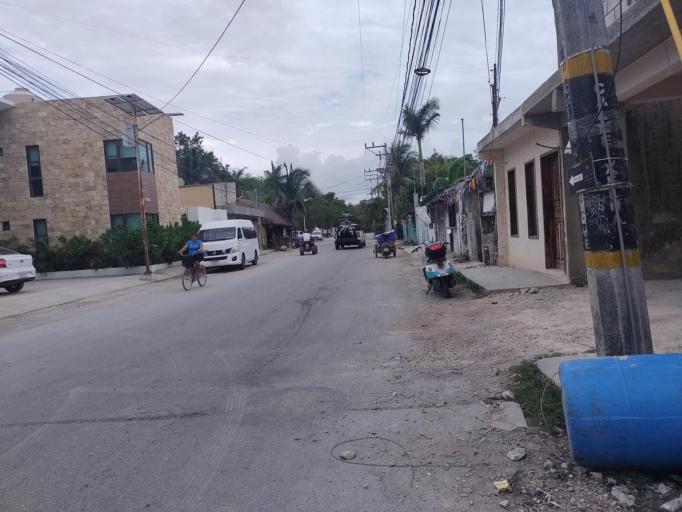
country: MX
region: Quintana Roo
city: Tulum
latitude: 20.2066
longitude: -87.4717
